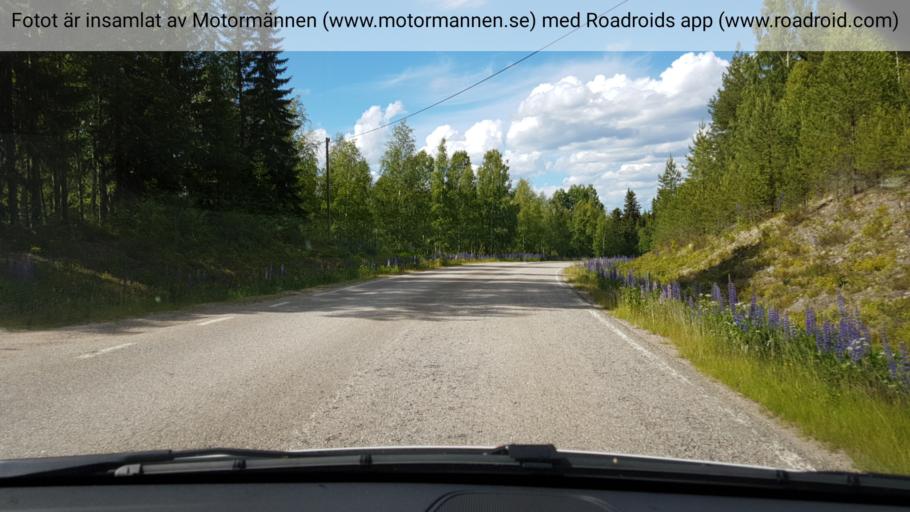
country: SE
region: Jaemtland
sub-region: Braecke Kommun
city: Braecke
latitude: 62.3798
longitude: 15.1694
